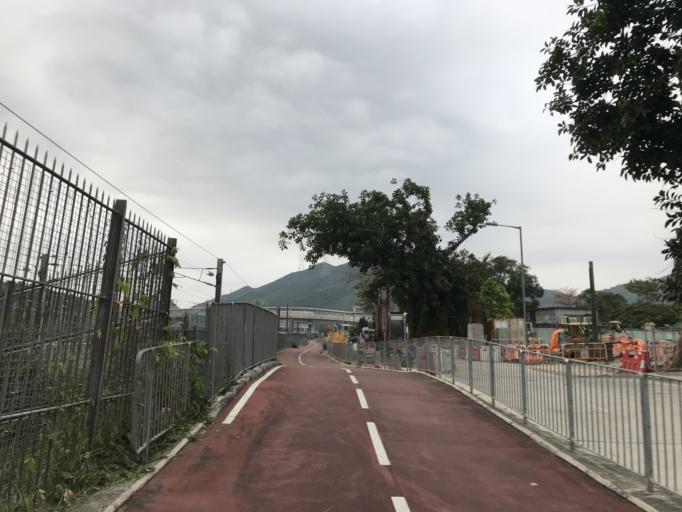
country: HK
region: Tai Po
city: Tai Po
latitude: 22.4729
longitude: 114.1540
